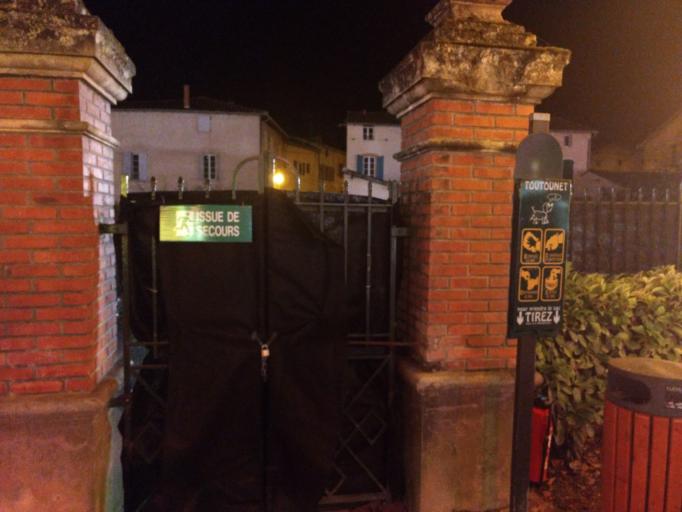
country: FR
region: Midi-Pyrenees
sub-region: Departement du Tarn
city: Gaillac
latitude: 43.8959
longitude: 1.8984
